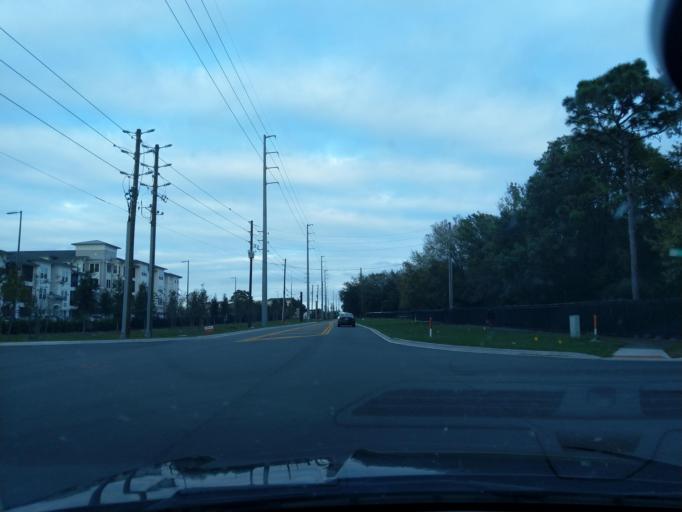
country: US
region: Florida
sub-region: Orange County
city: Doctor Phillips
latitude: 28.3913
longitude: -81.5016
